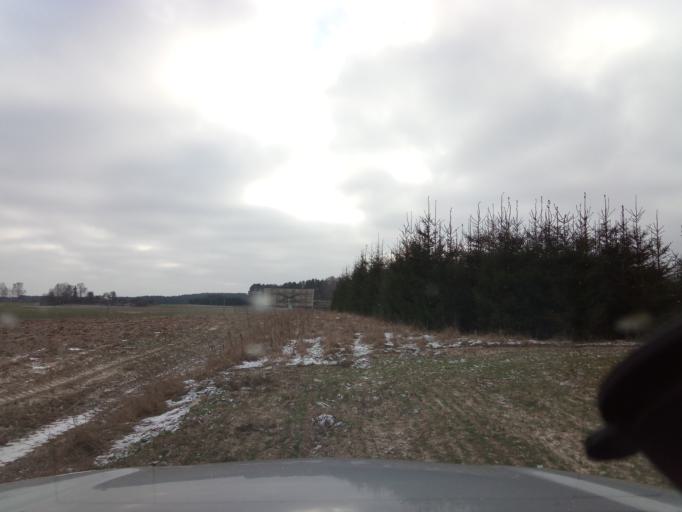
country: LT
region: Alytaus apskritis
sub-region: Alytaus rajonas
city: Daugai
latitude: 54.3163
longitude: 24.3705
